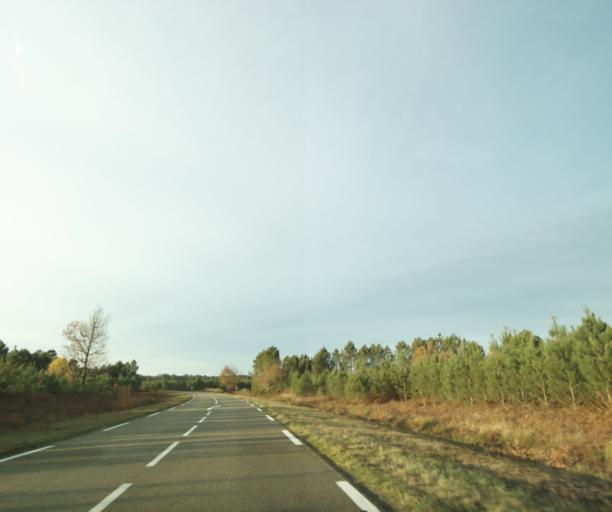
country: FR
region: Aquitaine
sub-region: Departement des Landes
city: Gabarret
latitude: 44.0847
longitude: -0.0744
